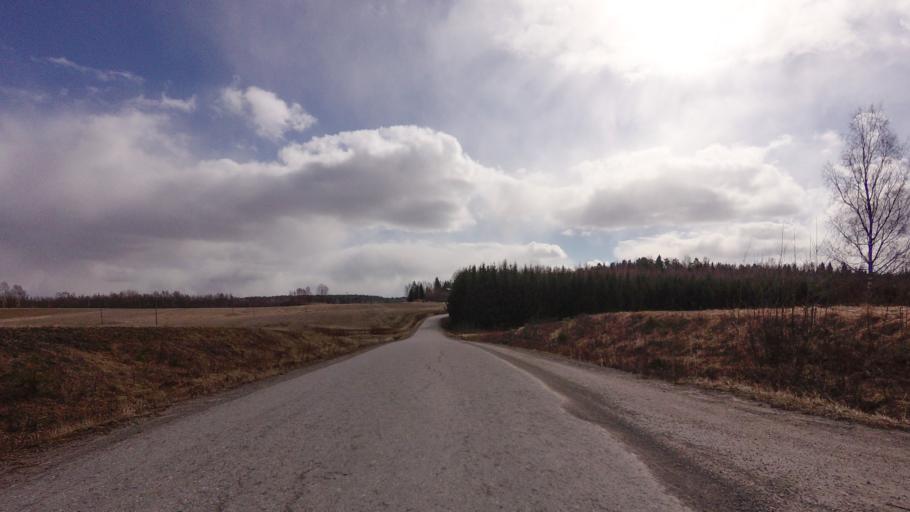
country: FI
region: Uusimaa
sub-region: Helsinki
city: Sammatti
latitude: 60.3046
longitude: 23.7505
